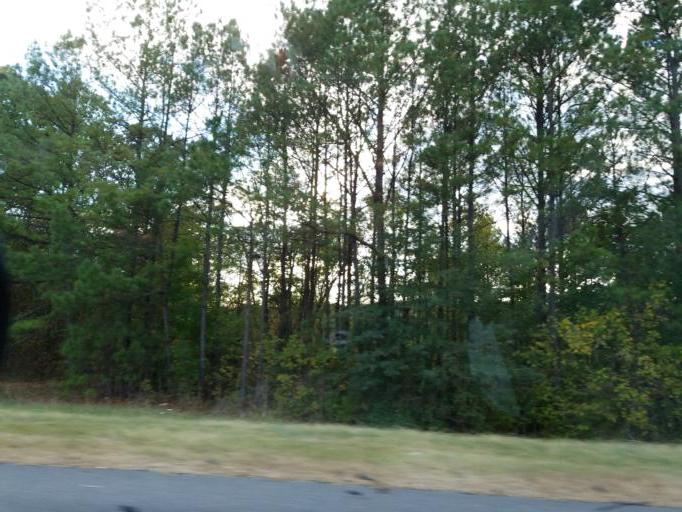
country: US
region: Georgia
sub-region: Bartow County
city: Emerson
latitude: 34.0992
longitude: -84.7264
